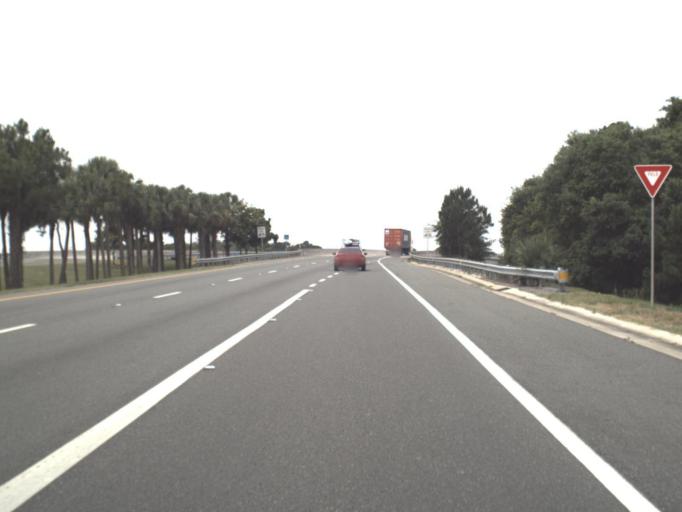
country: US
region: Florida
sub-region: Duval County
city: Jacksonville
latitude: 30.4136
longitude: -81.5461
